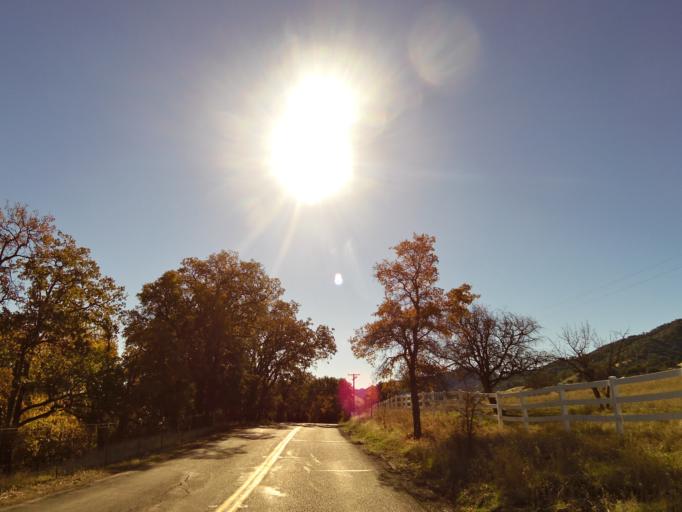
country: US
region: California
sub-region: Solano County
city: Vacaville
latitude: 38.4322
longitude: -122.0500
